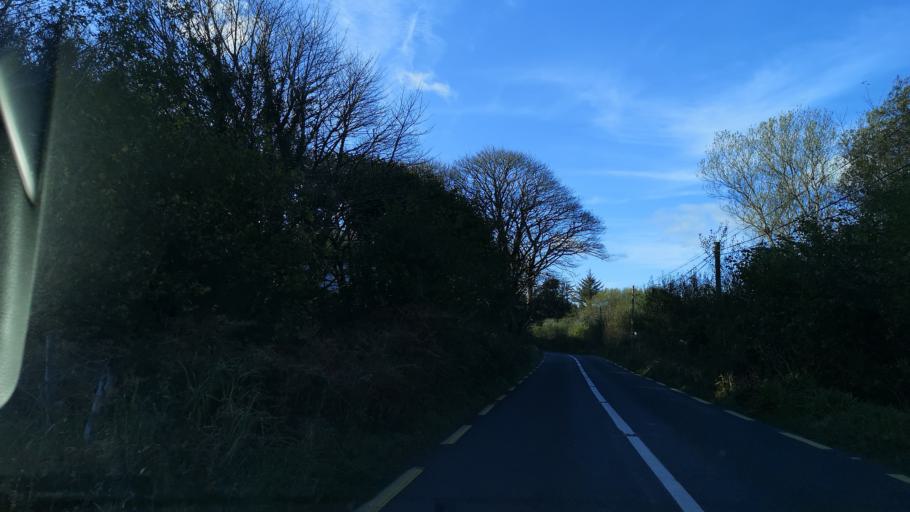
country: IE
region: Connaught
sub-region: County Galway
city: Clifden
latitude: 53.5438
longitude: -9.9929
